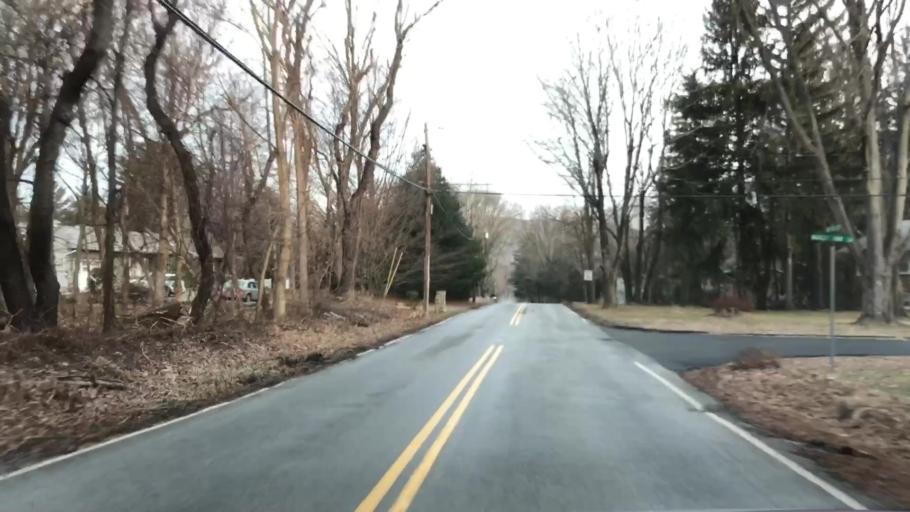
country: US
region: New York
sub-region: Rockland County
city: Viola
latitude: 41.1440
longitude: -74.0982
